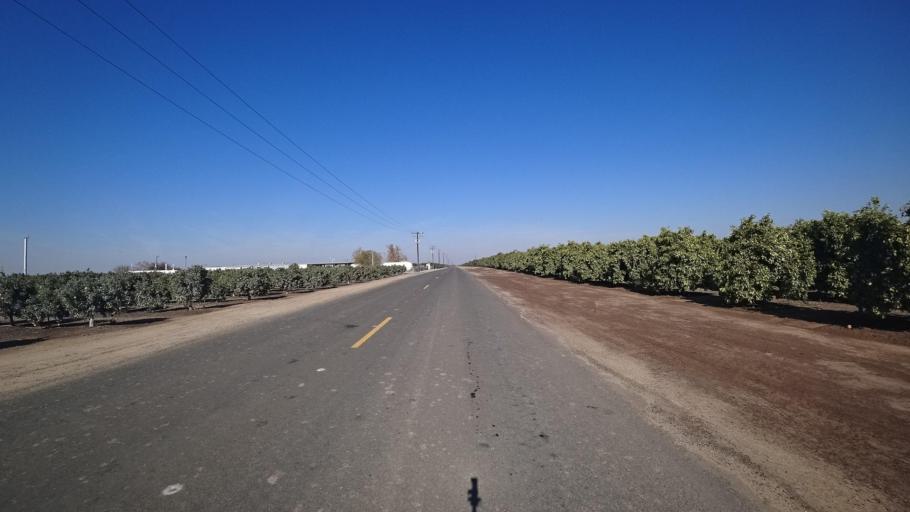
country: US
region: California
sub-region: Tulare County
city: Richgrove
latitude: 35.7219
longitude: -119.1340
